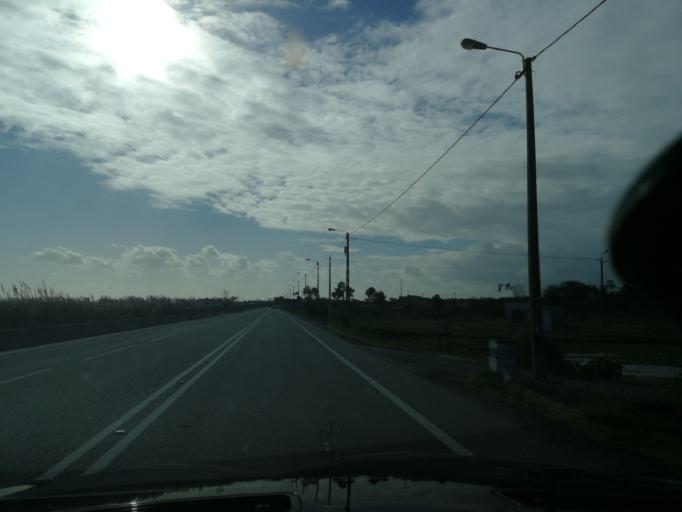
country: PT
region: Aveiro
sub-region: Estarreja
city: Pardilho
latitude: 40.7862
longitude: -8.6829
